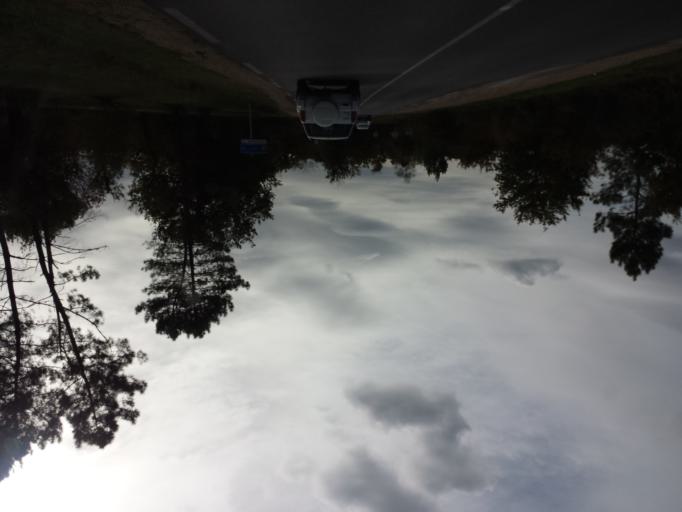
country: FR
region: Aquitaine
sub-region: Departement de la Gironde
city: Marcheprime
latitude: 44.7812
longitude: -0.9318
